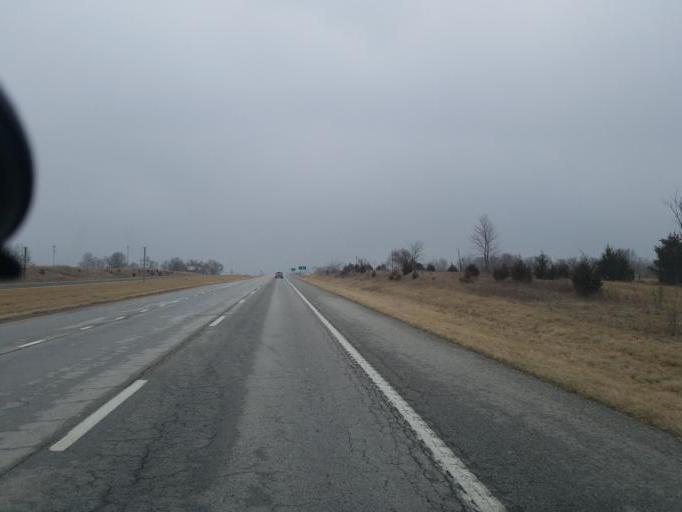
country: US
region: Missouri
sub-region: Macon County
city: La Plata
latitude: 39.9026
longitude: -92.4727
